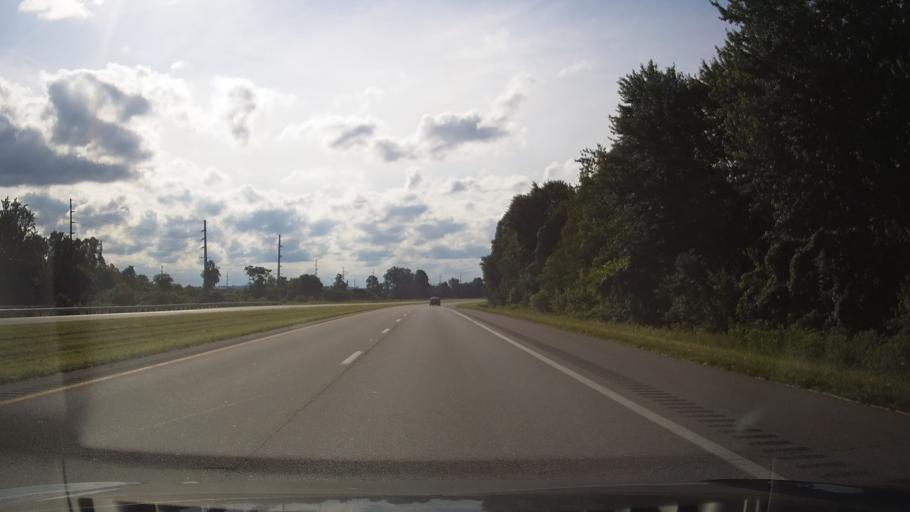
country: US
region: Kentucky
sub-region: Greenup County
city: Greenup
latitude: 38.5806
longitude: -82.7924
